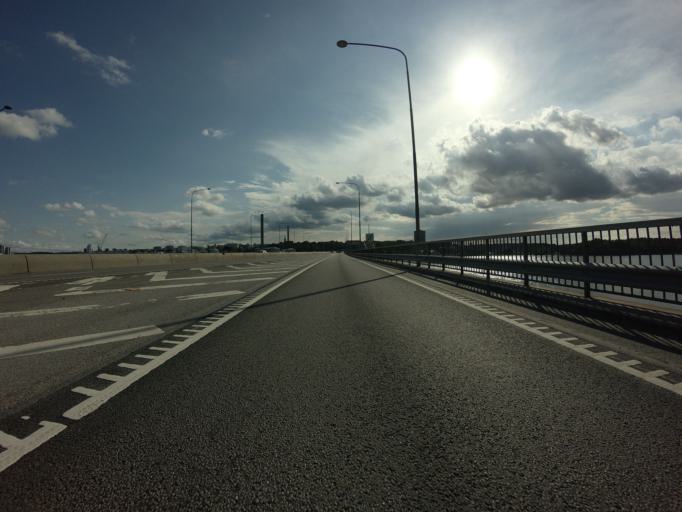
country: SE
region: Stockholm
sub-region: Lidingo
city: Lidingoe
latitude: 59.3618
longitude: 18.1130
